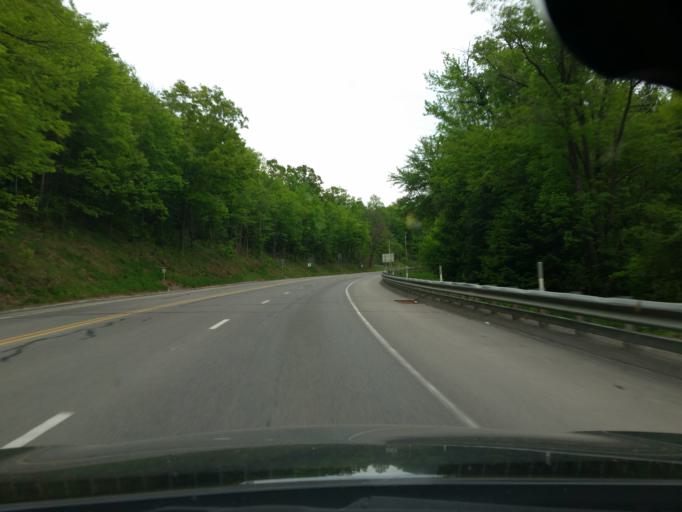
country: US
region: Pennsylvania
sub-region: Elk County
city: Ridgway
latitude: 41.4187
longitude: -78.7156
